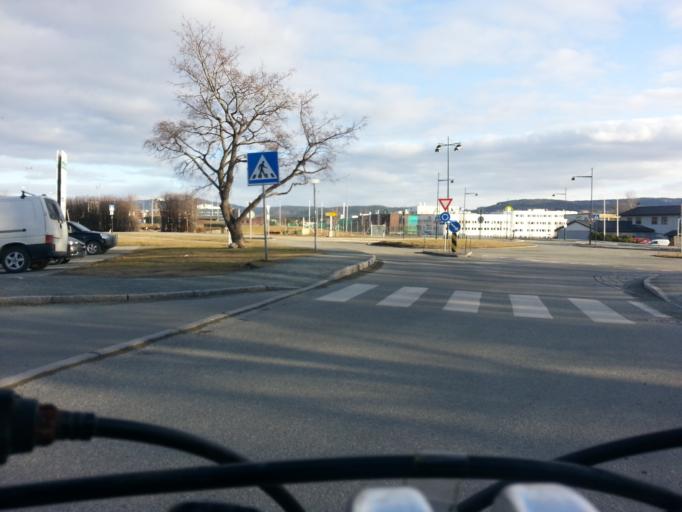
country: NO
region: Sor-Trondelag
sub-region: Trondheim
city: Trondheim
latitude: 63.4466
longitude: 10.4428
